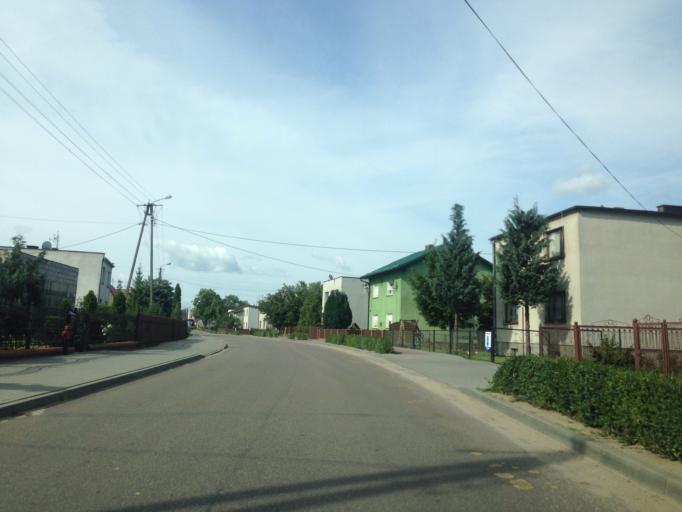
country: PL
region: Kujawsko-Pomorskie
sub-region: Powiat tucholski
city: Sliwice
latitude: 53.7140
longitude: 18.1806
